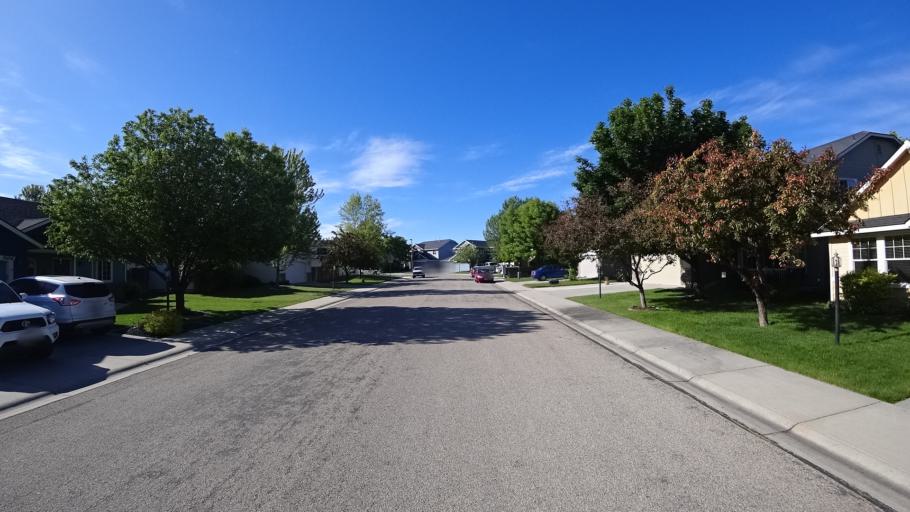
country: US
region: Idaho
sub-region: Ada County
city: Garden City
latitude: 43.5694
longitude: -116.2787
